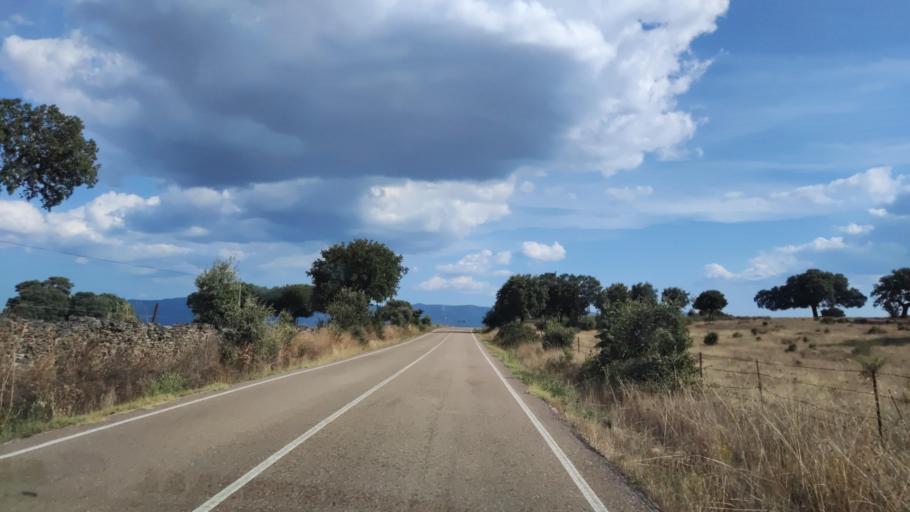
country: ES
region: Castille and Leon
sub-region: Provincia de Salamanca
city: Pastores
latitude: 40.4875
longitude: -6.4944
